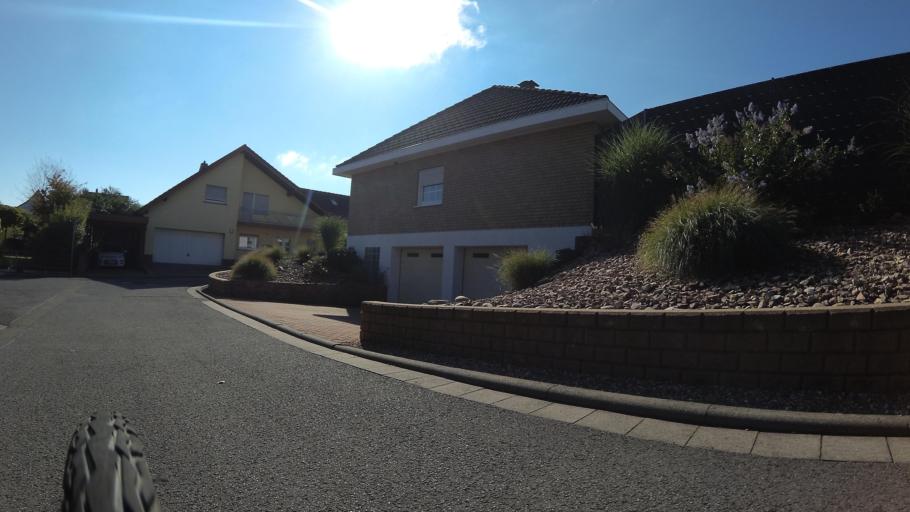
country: DE
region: Rheinland-Pfalz
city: Waldmohr
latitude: 49.3855
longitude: 7.3242
